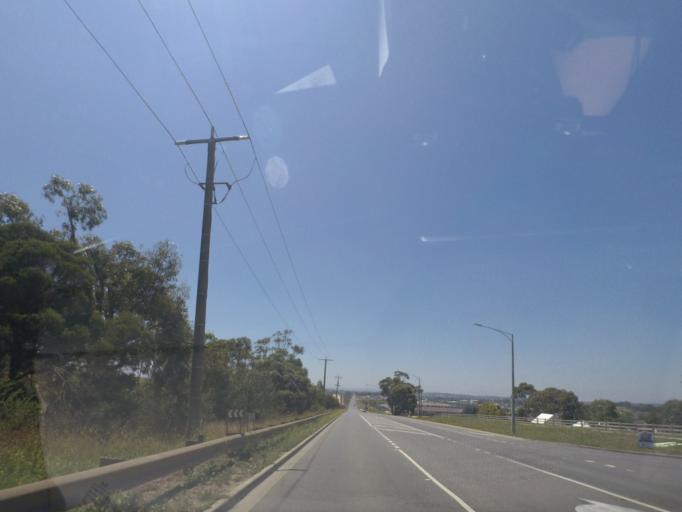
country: AU
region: Victoria
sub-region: Whittlesea
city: Mernda
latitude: -37.5976
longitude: 145.0690
